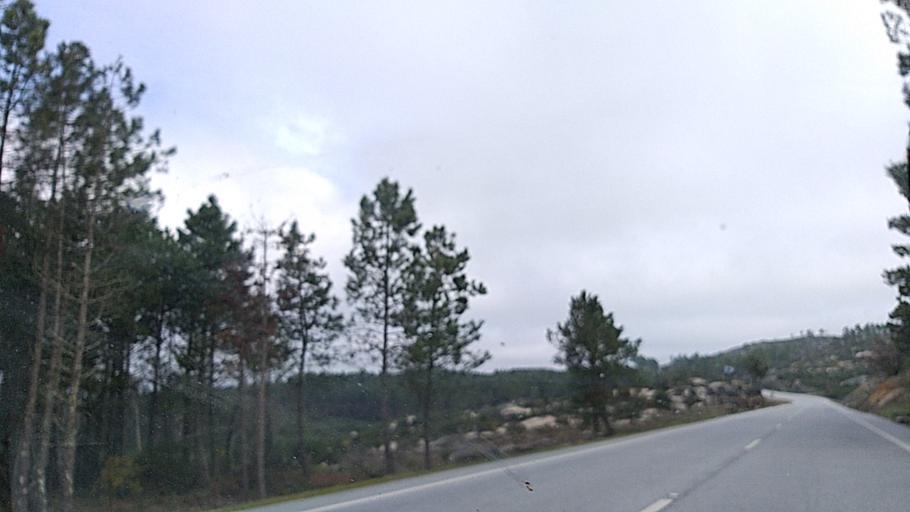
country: PT
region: Guarda
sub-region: Aguiar da Beira
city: Aguiar da Beira
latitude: 40.7552
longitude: -7.5038
